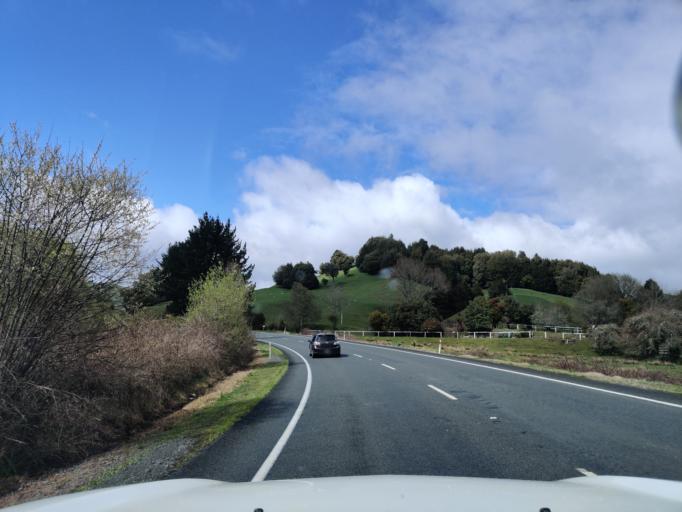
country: NZ
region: Waikato
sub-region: Otorohanga District
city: Otorohanga
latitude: -38.5854
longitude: 175.2152
